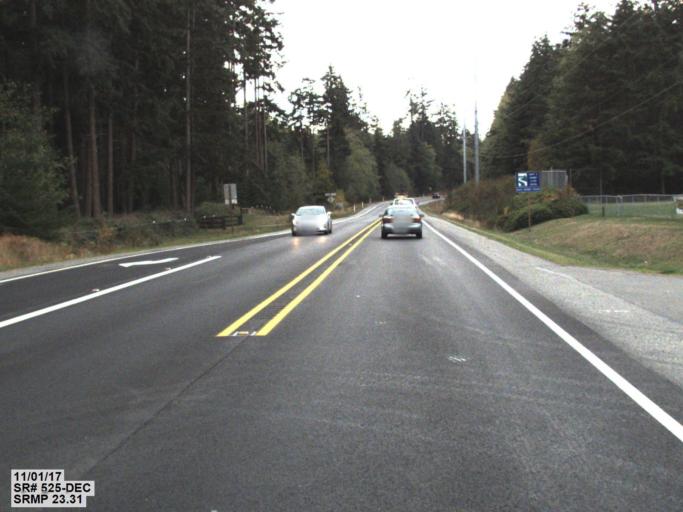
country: US
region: Washington
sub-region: Island County
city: Freeland
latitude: 48.0735
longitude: -122.5674
